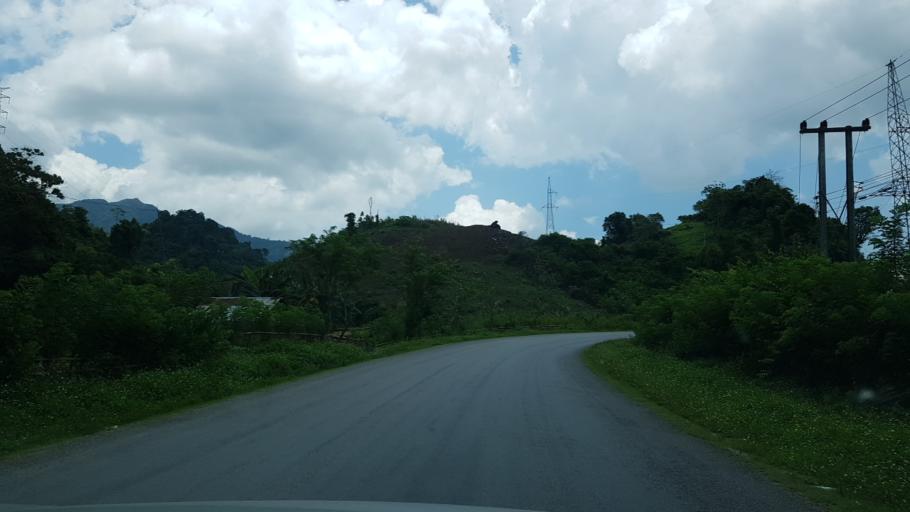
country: LA
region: Vientiane
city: Muang Kasi
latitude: 19.1400
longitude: 102.3036
